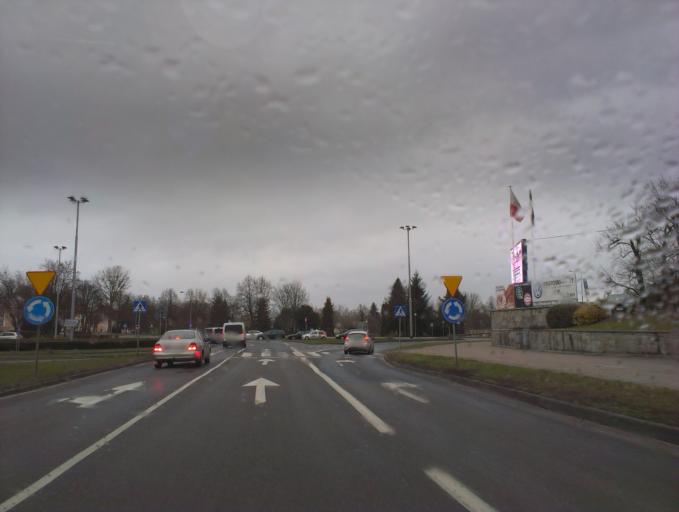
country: PL
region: Greater Poland Voivodeship
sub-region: Powiat pilski
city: Pila
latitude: 53.1505
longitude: 16.7383
